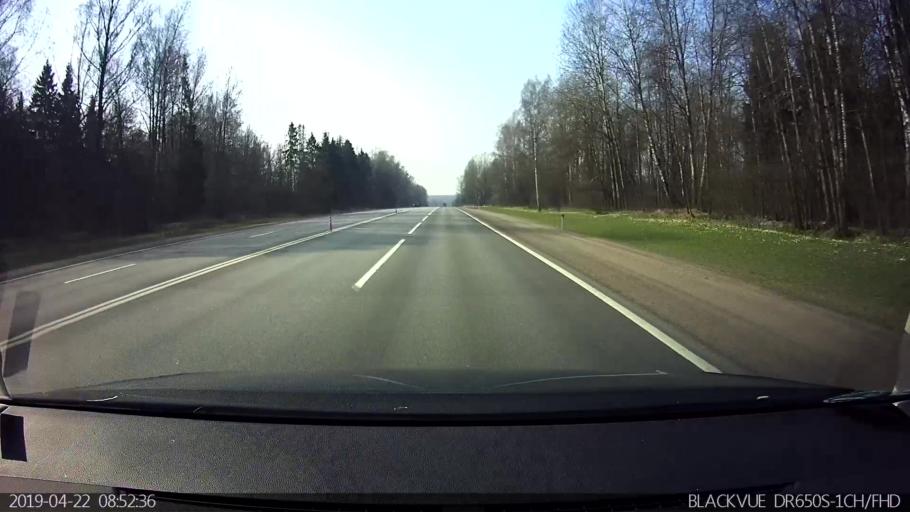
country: RU
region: Smolensk
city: Pechersk
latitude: 54.9071
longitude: 32.1235
